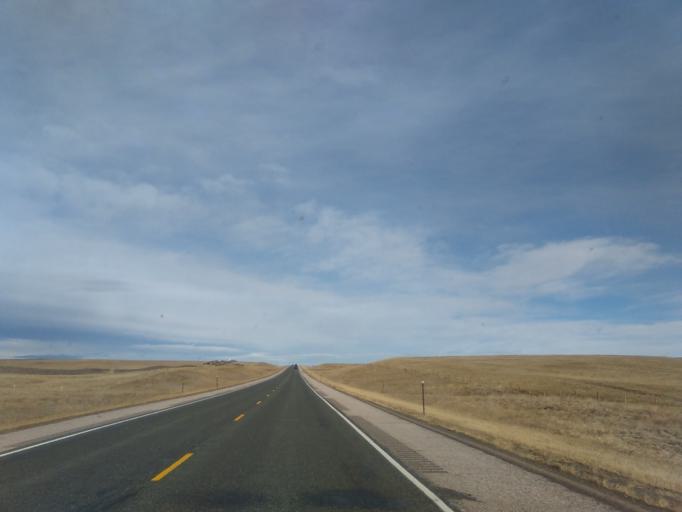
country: US
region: Wyoming
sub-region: Laramie County
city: Pine Bluffs
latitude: 41.5856
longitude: -104.2696
